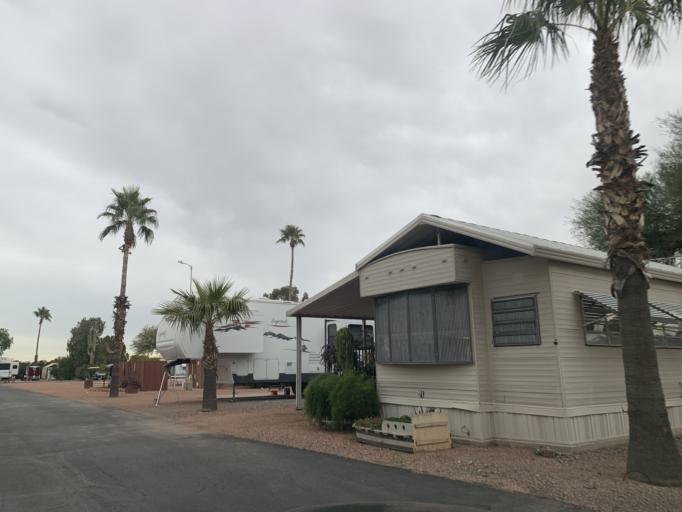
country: US
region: Arizona
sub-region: Pinal County
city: Arizona City
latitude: 32.8143
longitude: -111.6728
